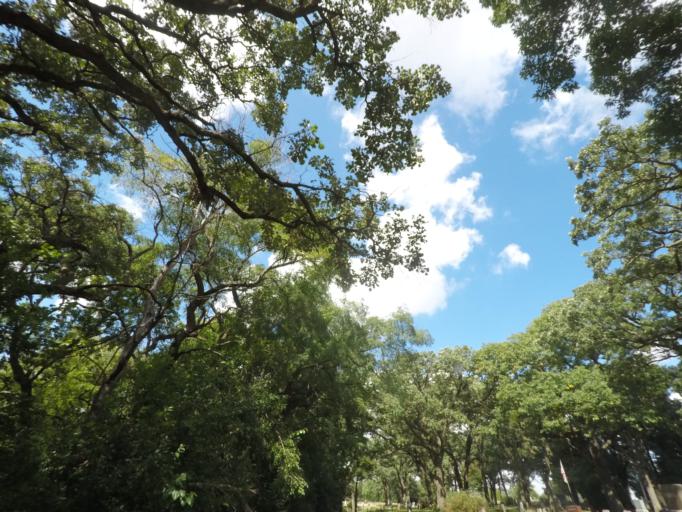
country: US
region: Iowa
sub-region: Story County
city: Nevada
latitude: 42.0205
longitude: -93.4638
